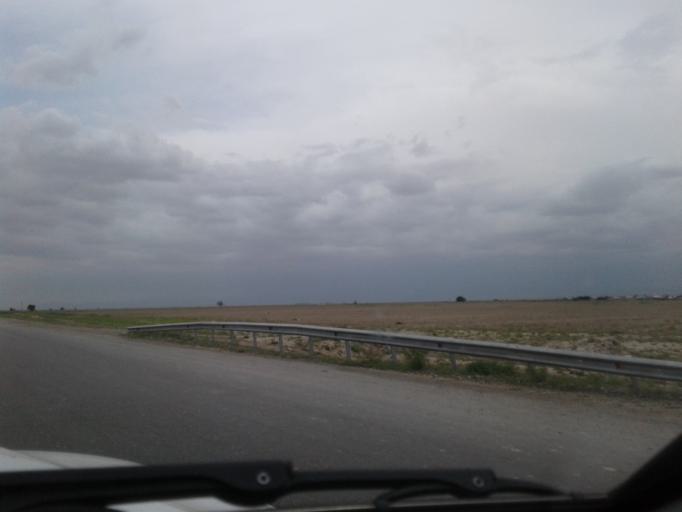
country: TM
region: Ahal
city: Kaka
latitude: 37.4723
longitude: 59.4968
